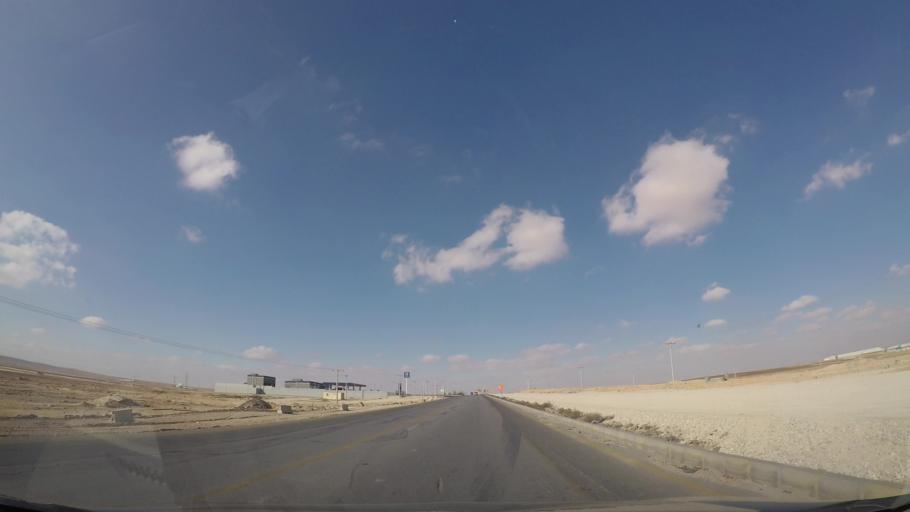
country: JO
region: Karak
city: Adir
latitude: 31.2778
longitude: 36.0543
